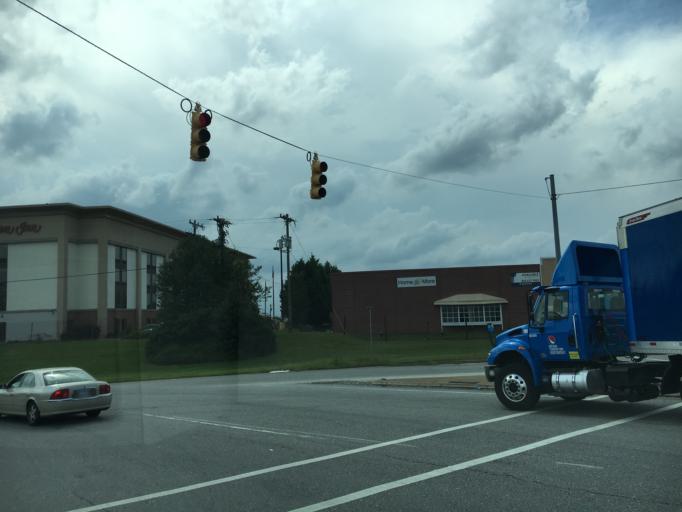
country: US
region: South Carolina
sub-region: Cherokee County
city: Gaffney
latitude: 35.0835
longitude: -81.7069
